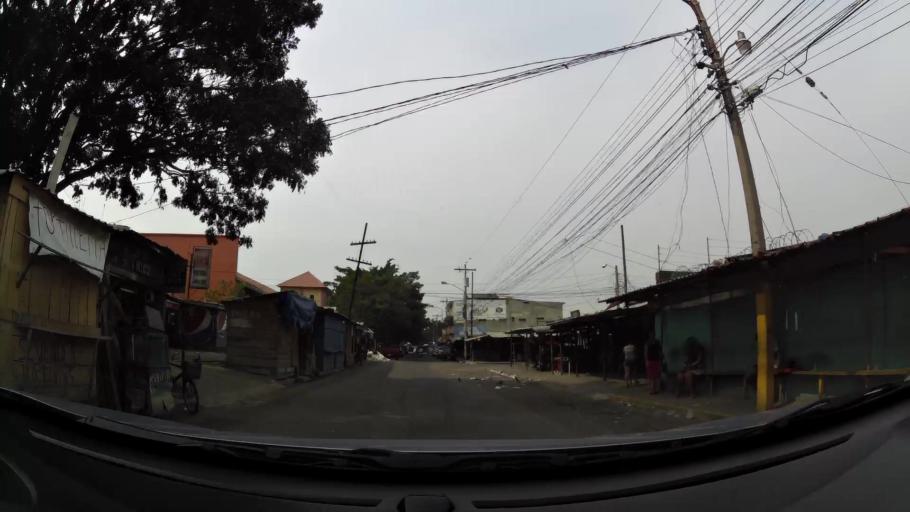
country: HN
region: Cortes
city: San Pedro Sula
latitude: 15.4991
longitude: -88.0237
